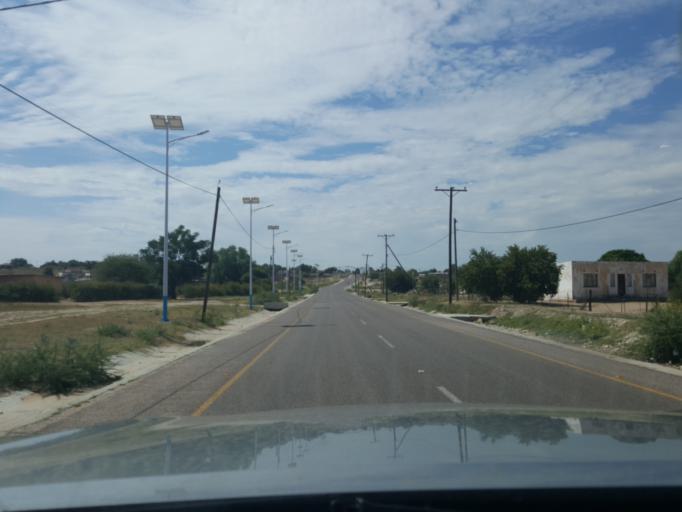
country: BW
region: Kweneng
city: Letlhakeng
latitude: -24.0927
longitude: 25.0301
